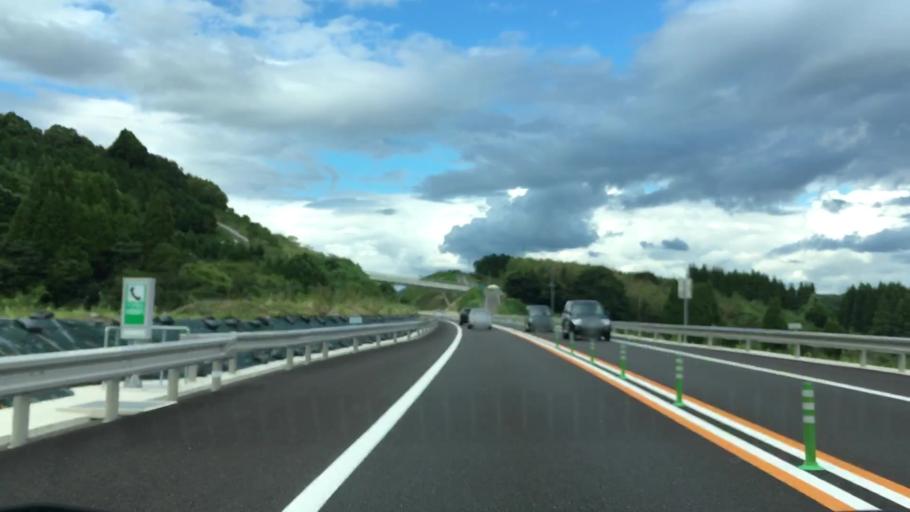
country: JP
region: Saga Prefecture
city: Imaricho-ko
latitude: 33.3191
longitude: 129.9245
